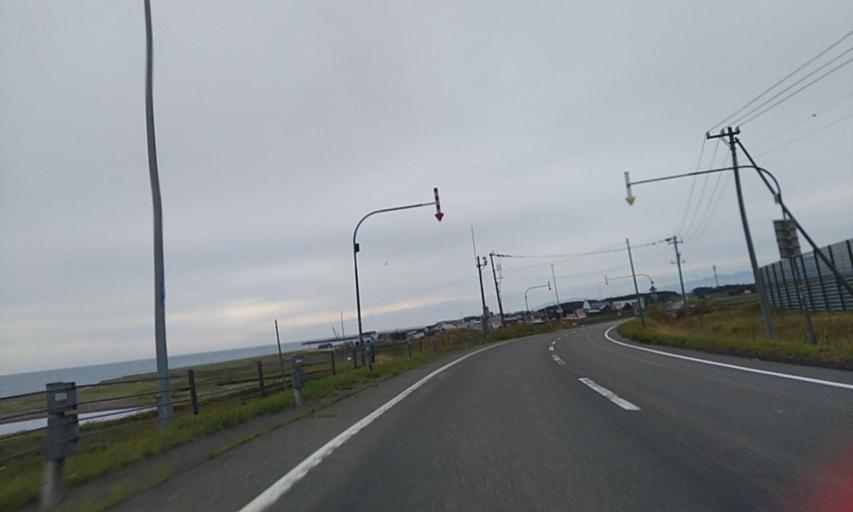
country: JP
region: Hokkaido
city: Makubetsu
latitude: 45.2805
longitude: 142.2243
